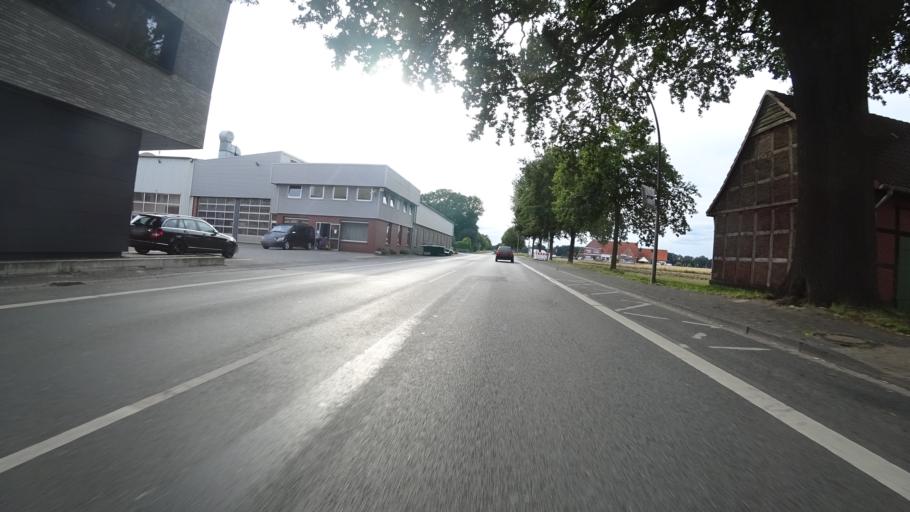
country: DE
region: North Rhine-Westphalia
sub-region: Regierungsbezirk Munster
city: Beelen
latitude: 51.9789
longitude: 8.1361
